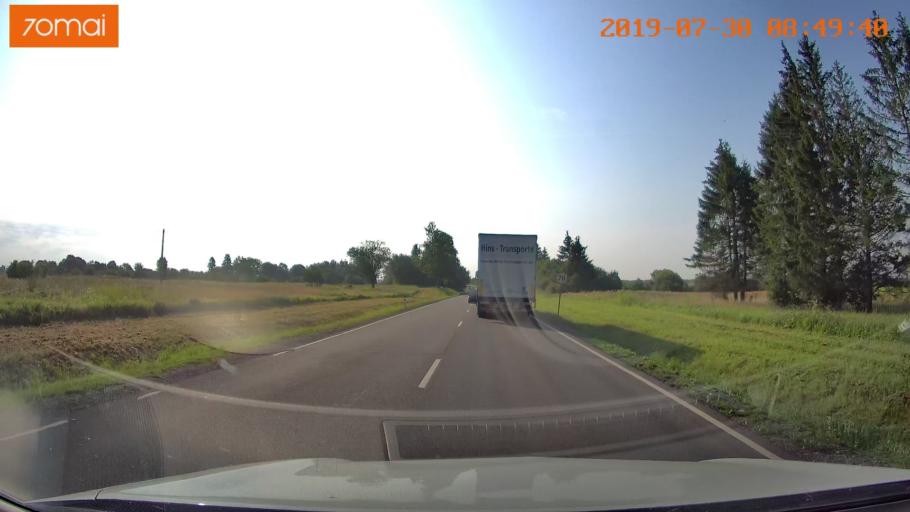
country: RU
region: Kaliningrad
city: Chernyakhovsk
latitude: 54.6119
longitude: 21.9260
